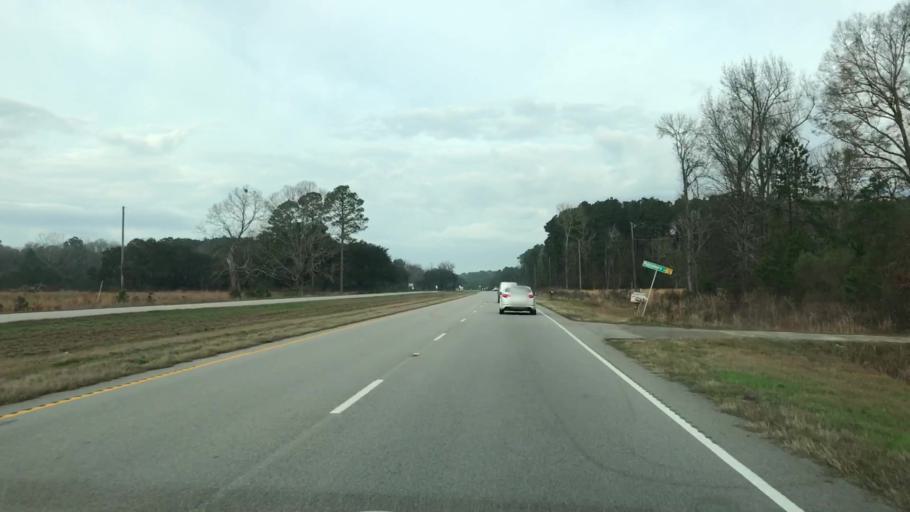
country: US
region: South Carolina
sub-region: Hampton County
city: Yemassee
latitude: 32.6358
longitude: -80.8424
